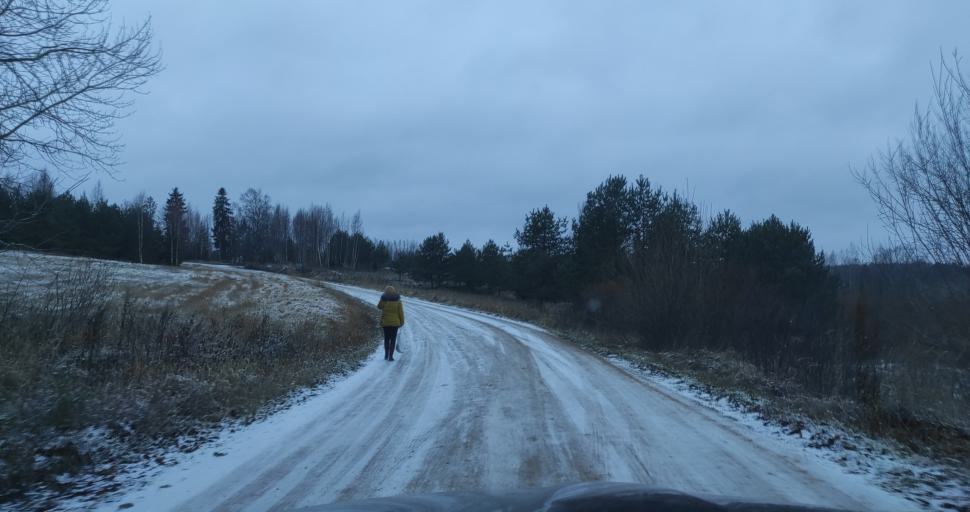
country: LV
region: Kuldigas Rajons
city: Kuldiga
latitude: 56.9815
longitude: 22.0512
